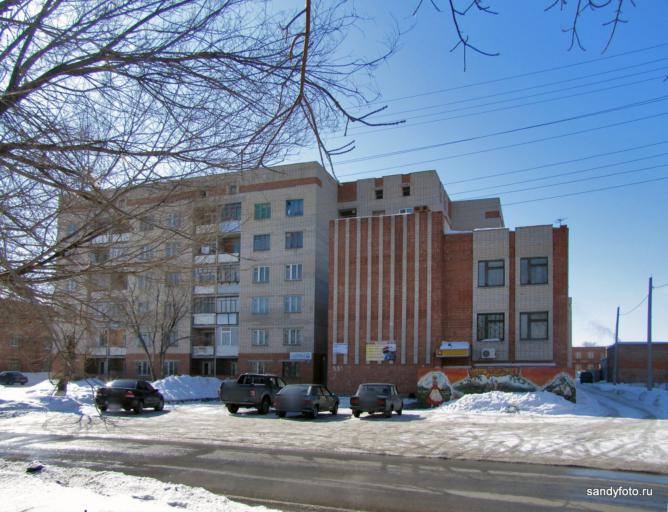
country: RU
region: Chelyabinsk
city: Troitsk
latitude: 54.0864
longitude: 61.5474
